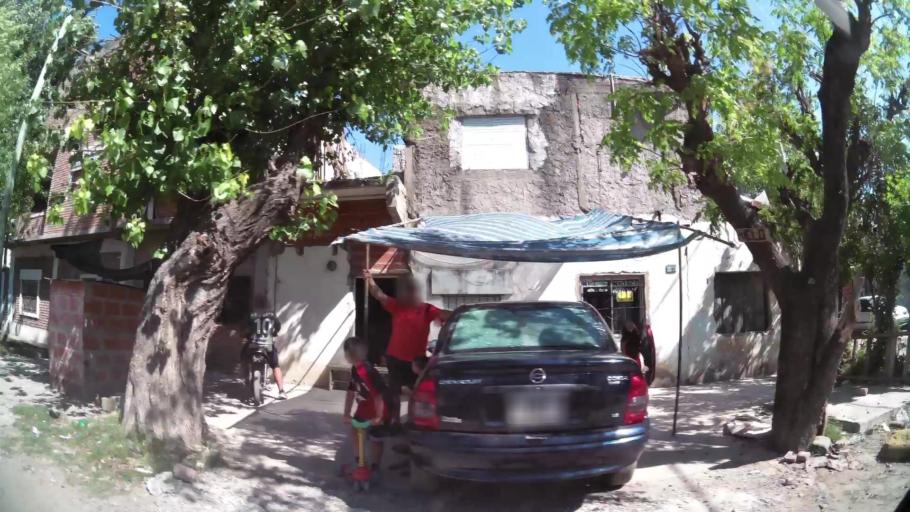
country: AR
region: Buenos Aires F.D.
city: Villa Lugano
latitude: -34.7045
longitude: -58.4707
